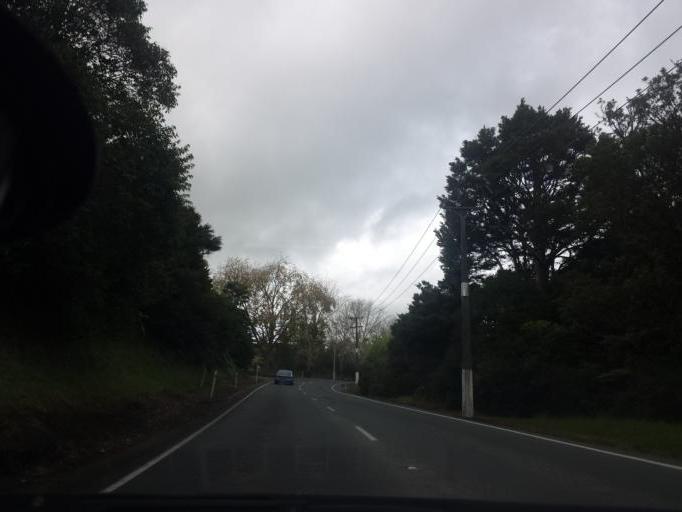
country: NZ
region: Auckland
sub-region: Auckland
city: Warkworth
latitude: -36.3938
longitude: 174.6644
